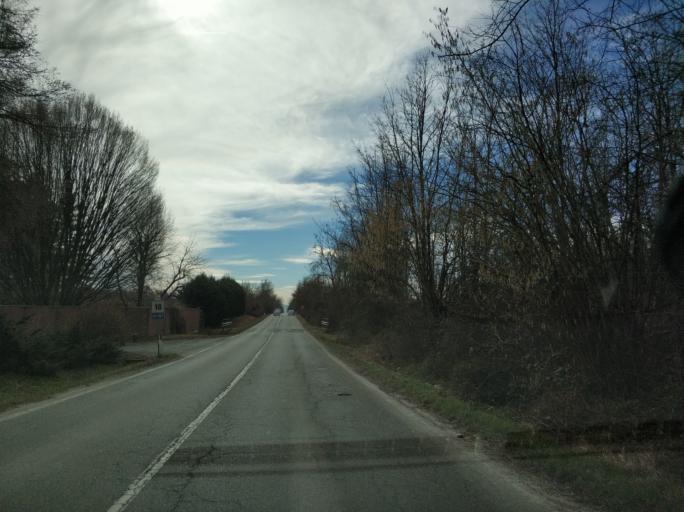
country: IT
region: Piedmont
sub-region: Provincia di Torino
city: Lombardore
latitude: 45.2227
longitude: 7.7311
